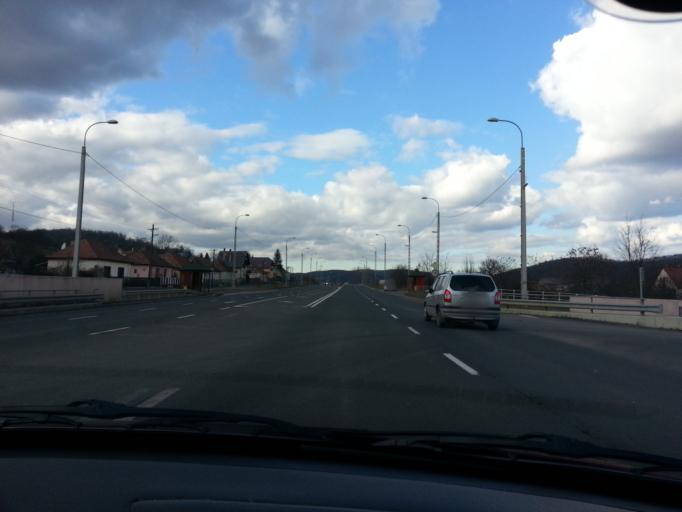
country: HU
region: Nograd
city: Kazar
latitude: 48.0357
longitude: 19.8027
